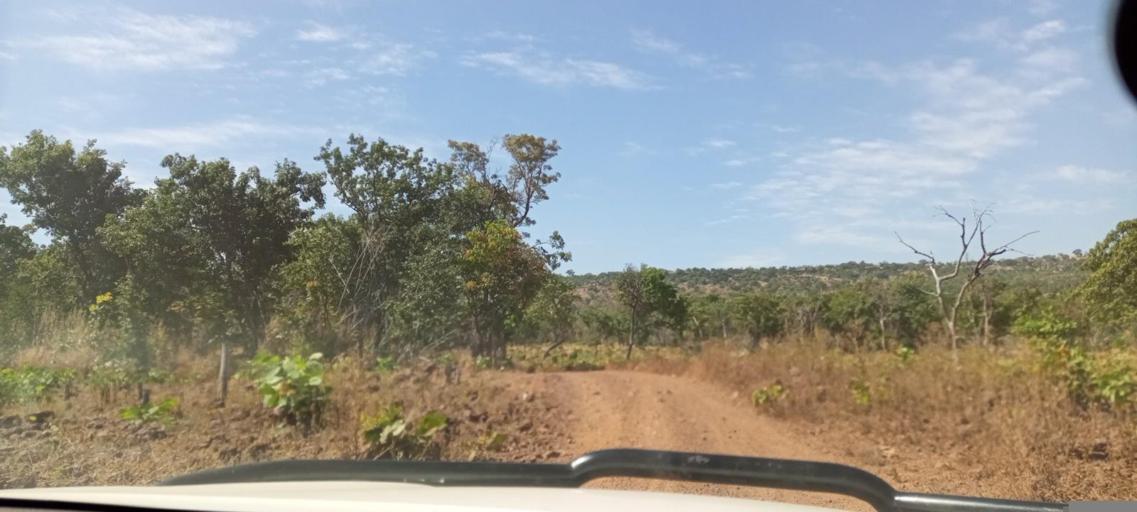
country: ML
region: Koulikoro
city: Kangaba
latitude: 12.3266
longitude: -8.6739
